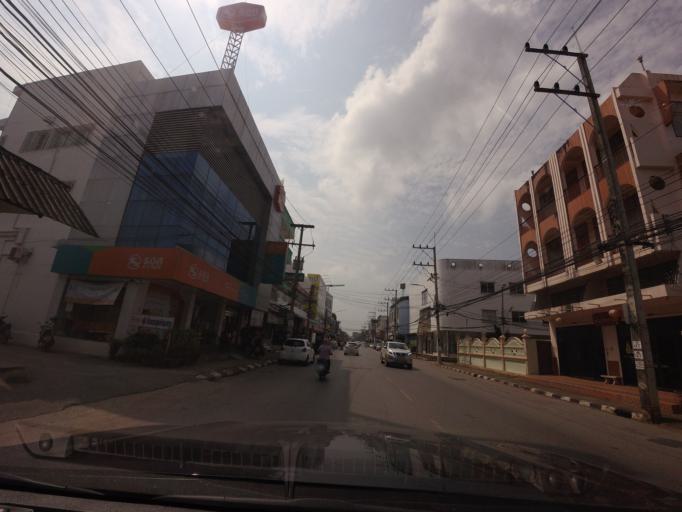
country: TH
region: Phrae
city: Phrae
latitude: 18.1456
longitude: 100.1489
